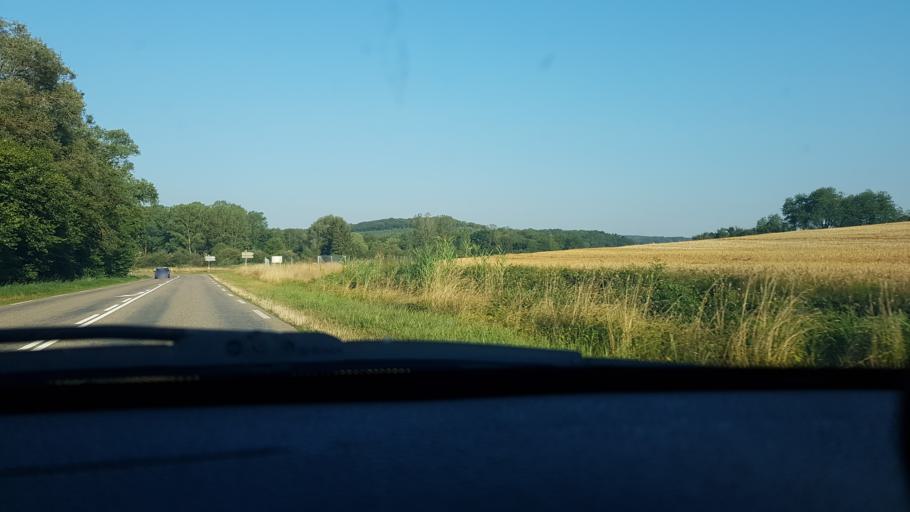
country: FR
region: Lorraine
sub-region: Departement des Vosges
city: Mirecourt
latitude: 48.3532
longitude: 6.1717
